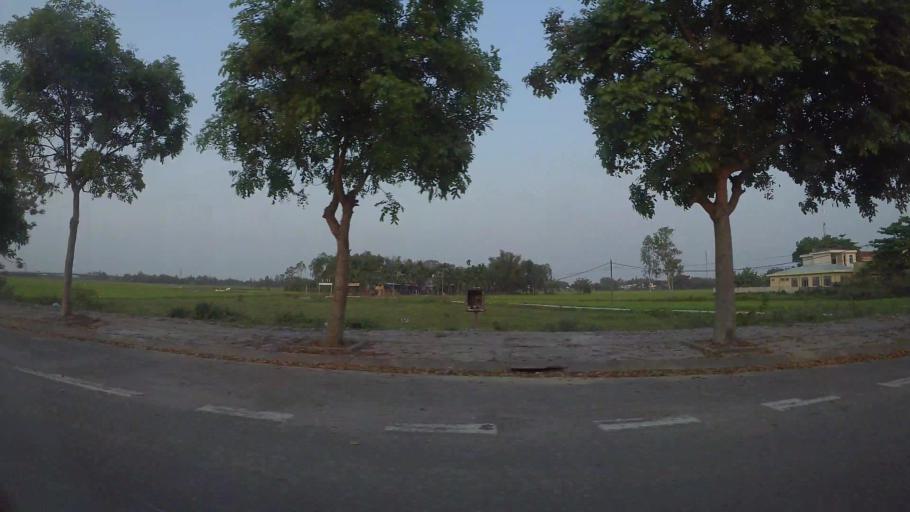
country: VN
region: Da Nang
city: Cam Le
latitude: 15.9595
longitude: 108.2146
